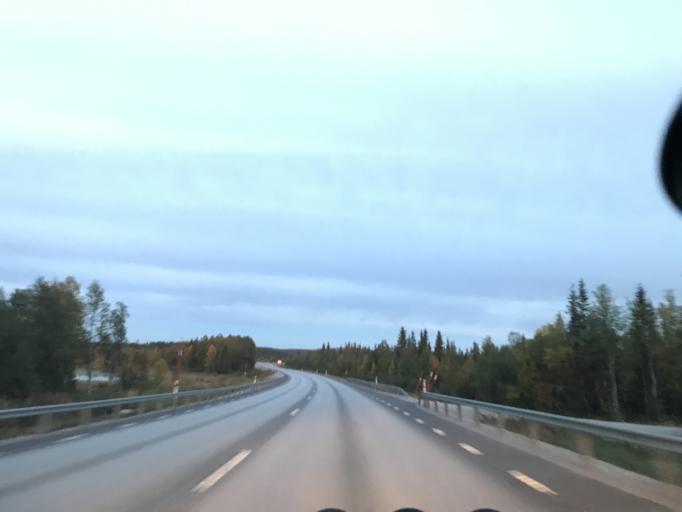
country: SE
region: Norrbotten
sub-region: Gallivare Kommun
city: Malmberget
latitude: 67.6471
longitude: 21.0287
